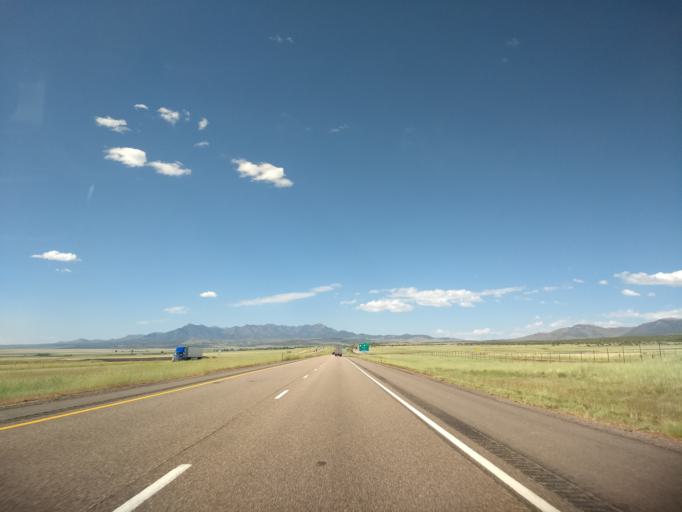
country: US
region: Utah
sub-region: Millard County
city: Fillmore
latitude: 39.0631
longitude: -112.2852
